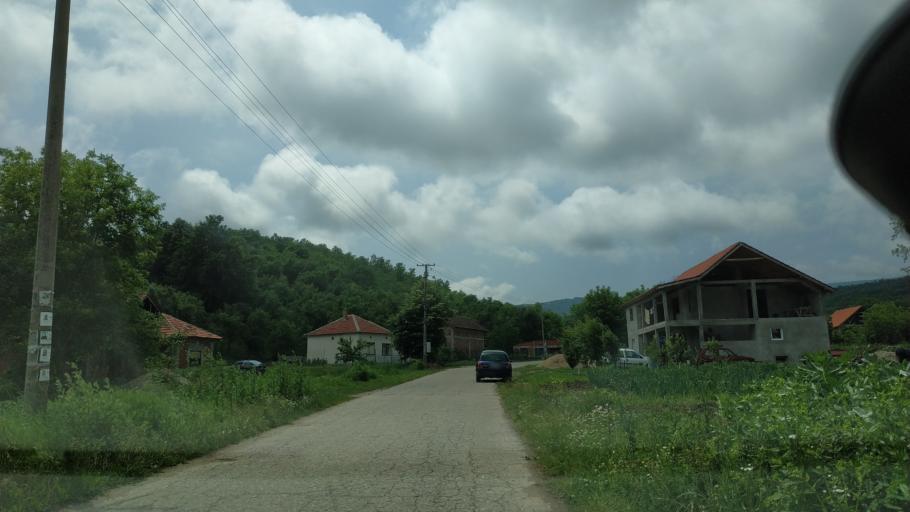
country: RS
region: Central Serbia
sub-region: Nisavski Okrug
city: Aleksinac
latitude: 43.4251
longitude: 21.7089
